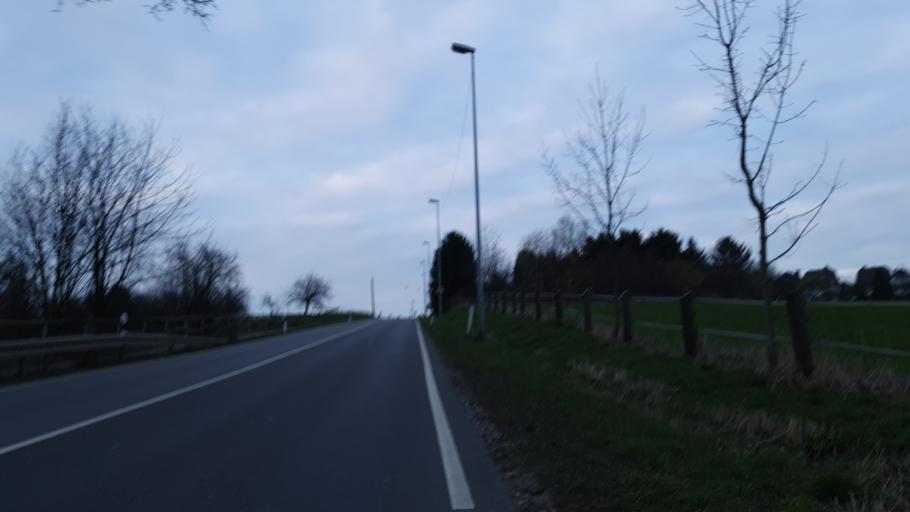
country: DE
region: North Rhine-Westphalia
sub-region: Regierungsbezirk Koln
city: Odenthal
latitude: 51.0617
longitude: 7.1122
